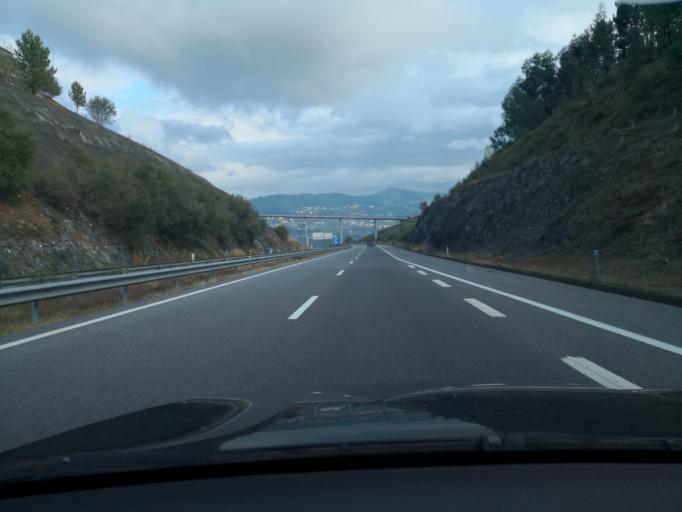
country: PT
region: Porto
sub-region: Felgueiras
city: Vizela
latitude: 41.3992
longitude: -8.2462
